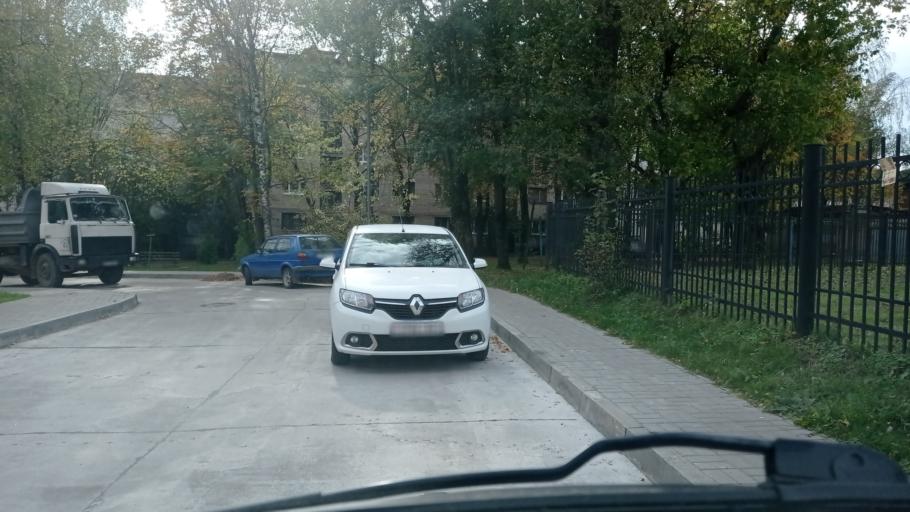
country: BY
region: Vitebsk
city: Vitebsk
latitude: 55.1840
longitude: 30.2127
